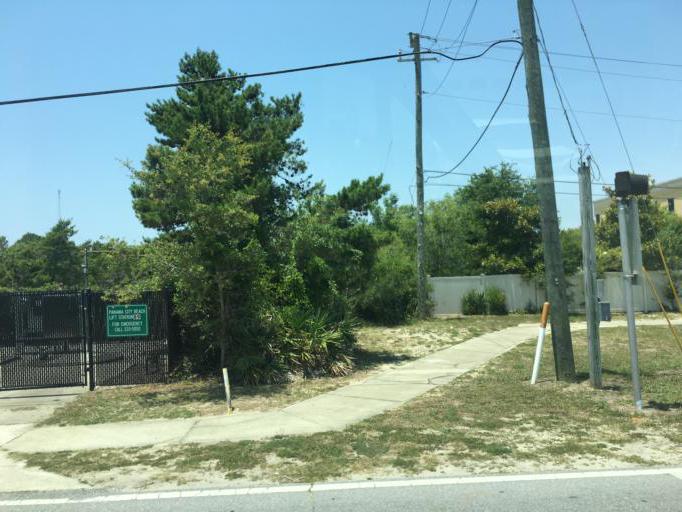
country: US
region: Florida
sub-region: Bay County
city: Panama City Beach
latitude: 30.2093
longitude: -85.8499
